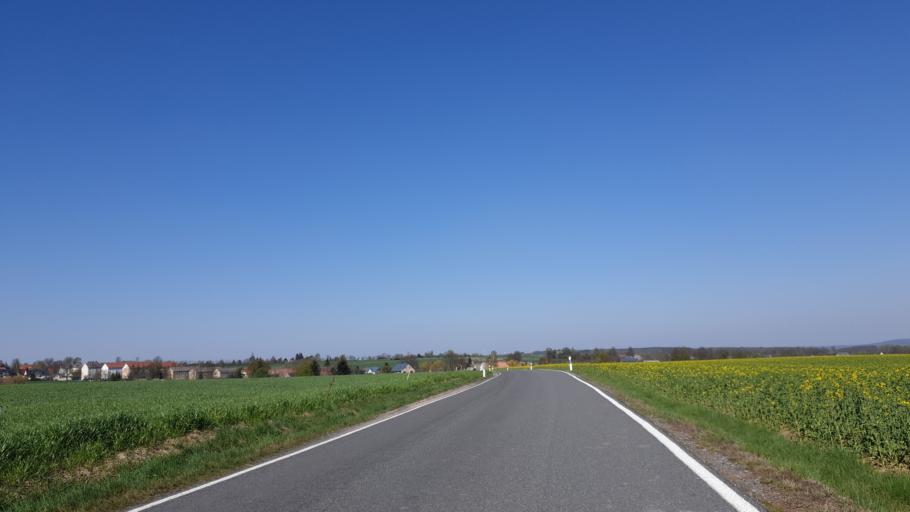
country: DE
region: Saxony
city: Taura
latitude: 50.9254
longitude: 12.8330
